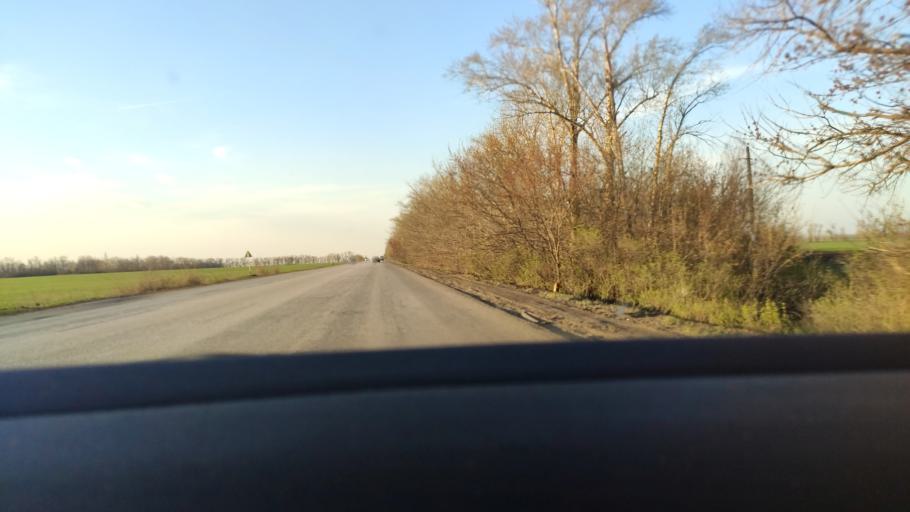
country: RU
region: Voronezj
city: Maslovka
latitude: 51.4374
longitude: 39.3022
